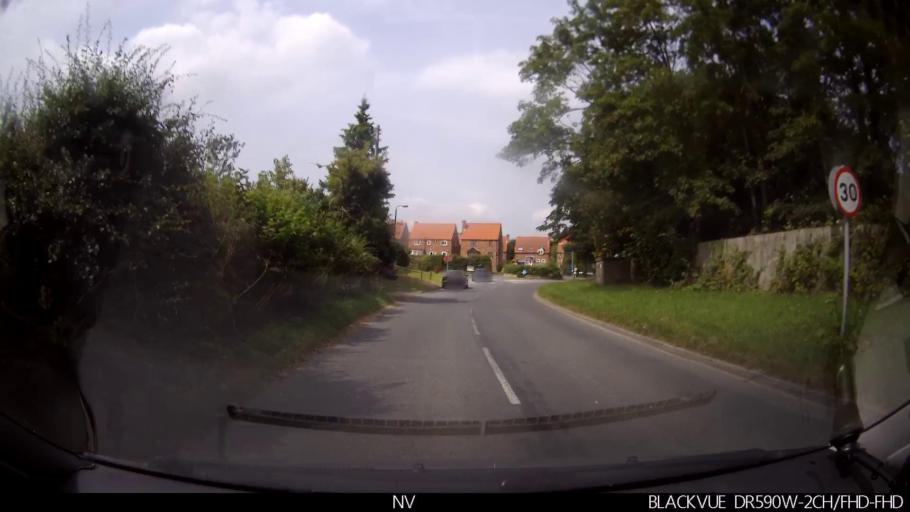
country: GB
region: England
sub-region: North Yorkshire
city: Great Habton
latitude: 54.2047
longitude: -0.8054
